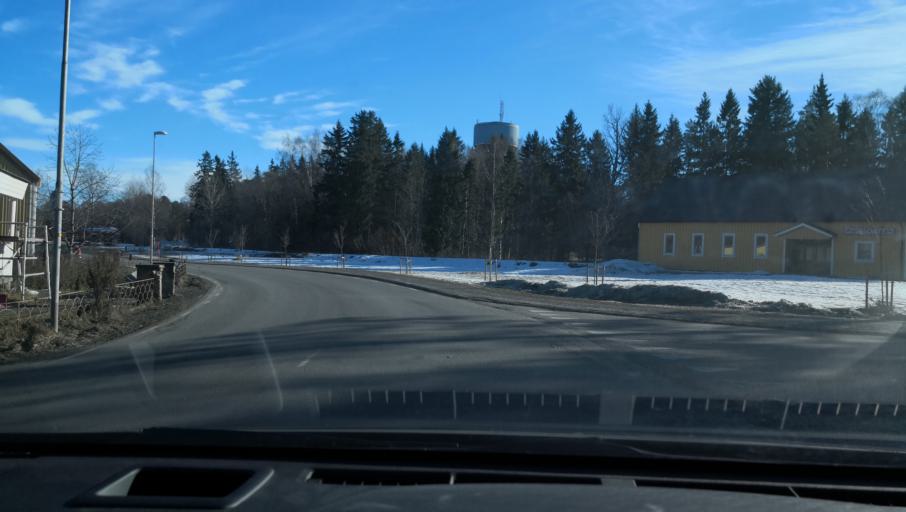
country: SE
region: Uppsala
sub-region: Osthammars Kommun
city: Osterbybruk
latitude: 60.1969
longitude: 17.8863
